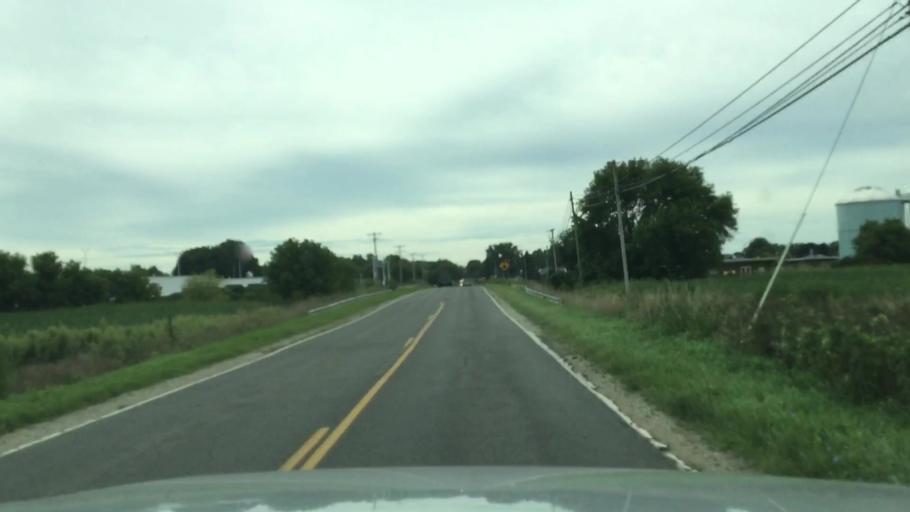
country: US
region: Michigan
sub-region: Shiawassee County
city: Durand
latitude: 42.9284
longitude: -83.9883
